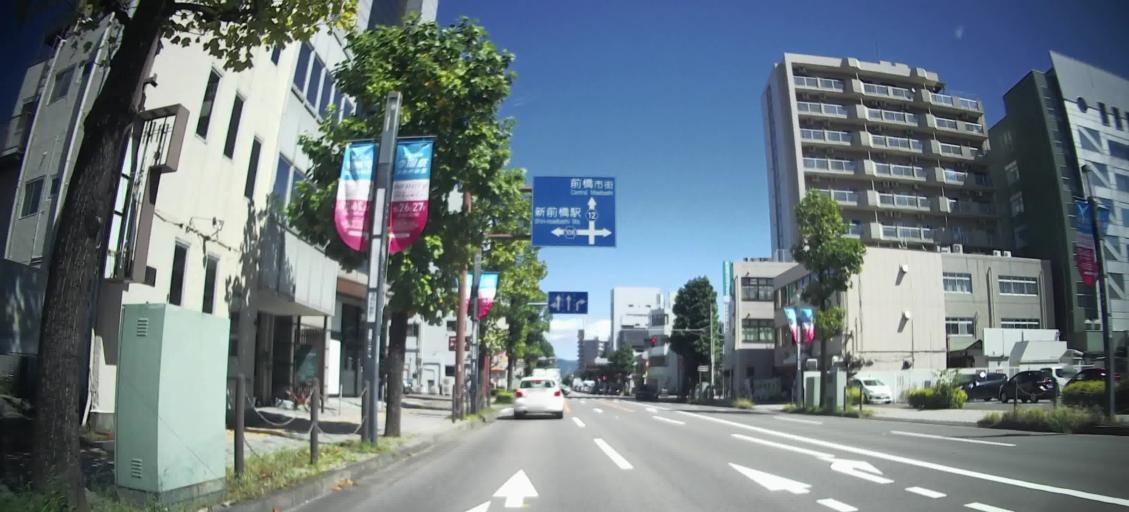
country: JP
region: Gunma
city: Maebashi-shi
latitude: 36.3774
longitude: 139.0474
